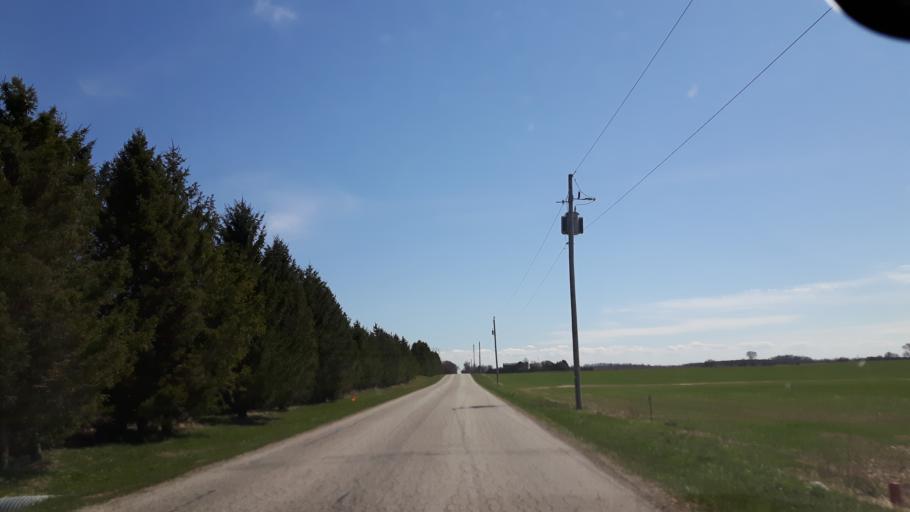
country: CA
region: Ontario
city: Goderich
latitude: 43.6415
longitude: -81.6440
